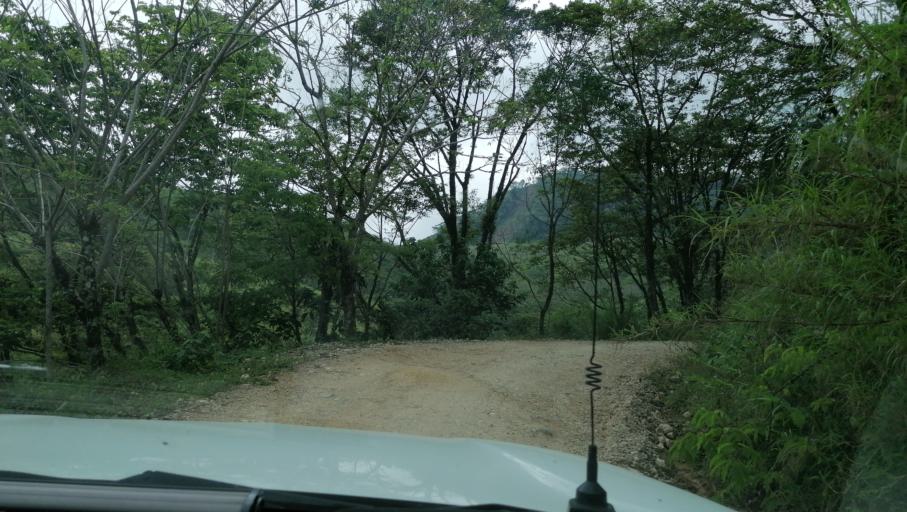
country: MX
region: Chiapas
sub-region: Ocotepec
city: San Pablo Huacano
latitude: 17.2697
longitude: -93.2449
